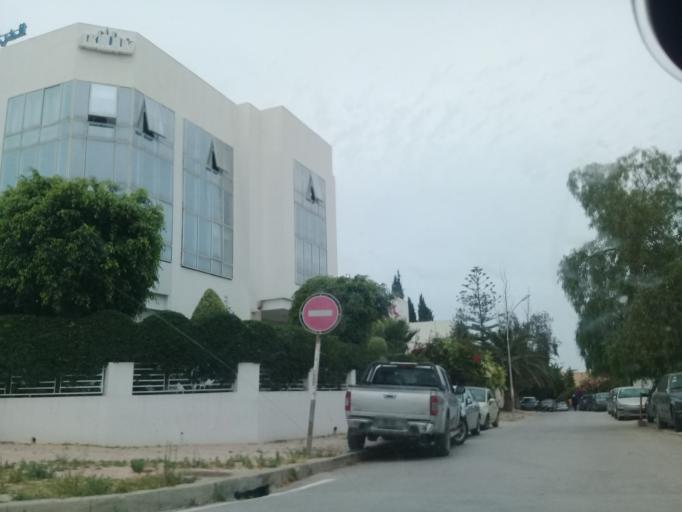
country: TN
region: Tunis
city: Tunis
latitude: 36.8427
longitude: 10.1548
